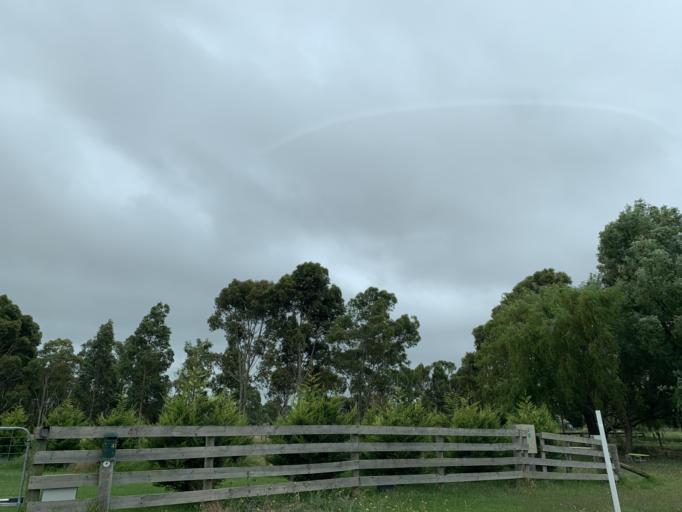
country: AU
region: Victoria
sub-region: Kingston
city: Chelsea Heights
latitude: -38.0259
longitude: 145.1674
